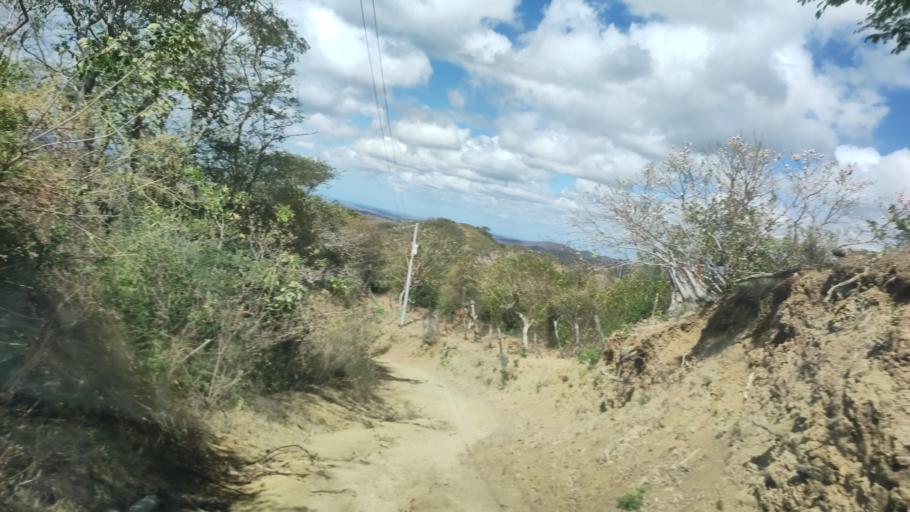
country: NI
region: Carazo
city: Santa Teresa
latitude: 11.6522
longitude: -86.2069
